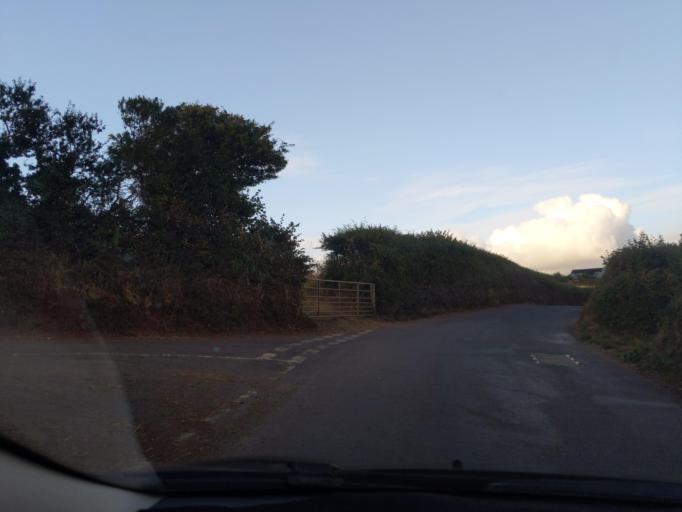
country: GB
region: England
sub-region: Devon
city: Salcombe
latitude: 50.2424
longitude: -3.8207
